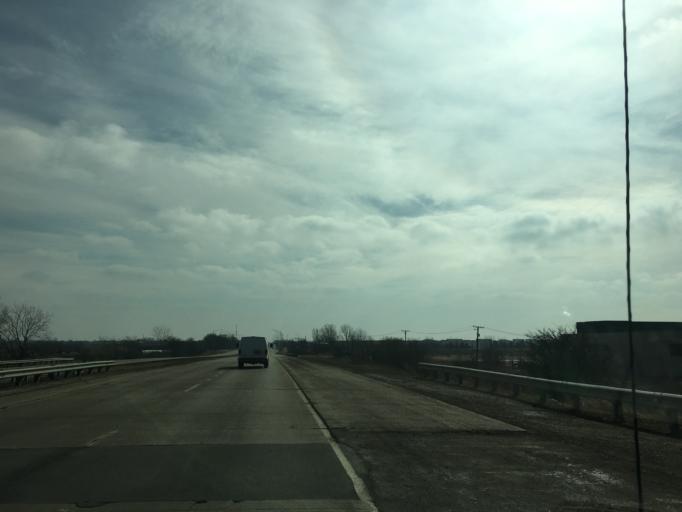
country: US
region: Illinois
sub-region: Cook County
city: Streamwood
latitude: 42.0775
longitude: -88.2008
